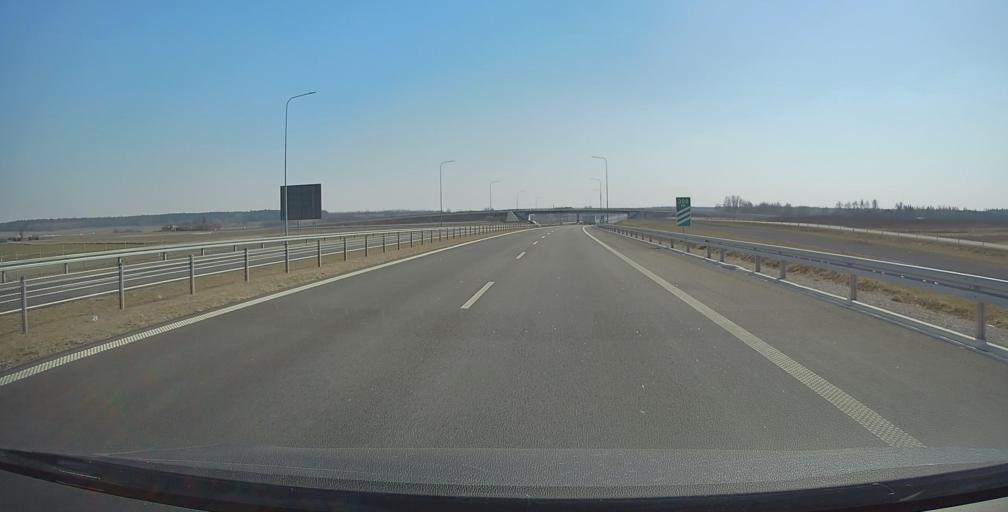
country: PL
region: Lublin Voivodeship
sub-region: Powiat janowski
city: Modliborzyce
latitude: 50.7344
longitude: 22.3452
